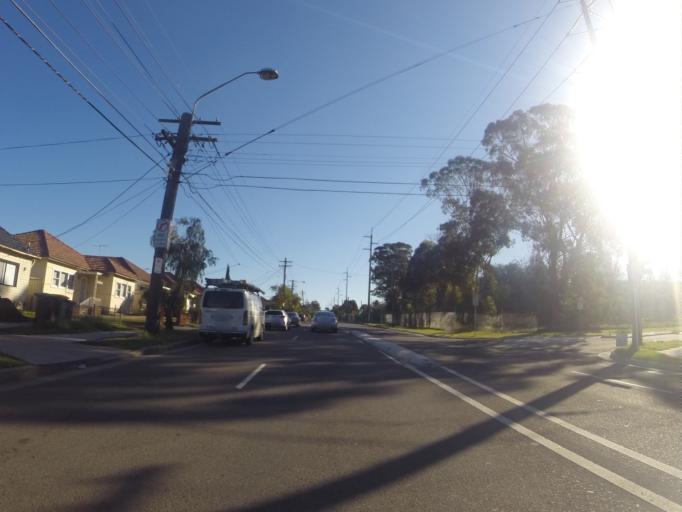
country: AU
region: New South Wales
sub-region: Bankstown
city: Bankstown
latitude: -33.8988
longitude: 151.0351
